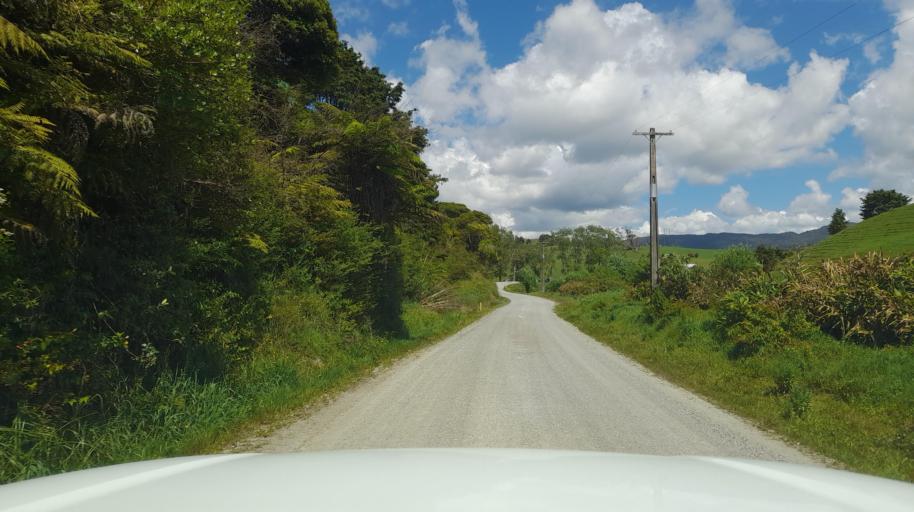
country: NZ
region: Northland
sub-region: Far North District
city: Taipa
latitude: -35.1229
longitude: 173.4079
